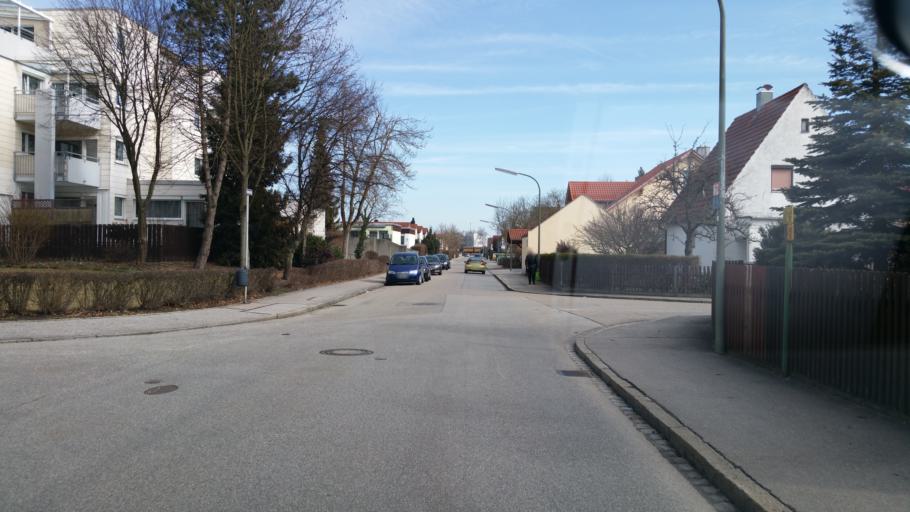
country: DE
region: Bavaria
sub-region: Lower Bavaria
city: Landshut
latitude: 48.5563
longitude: 12.1381
